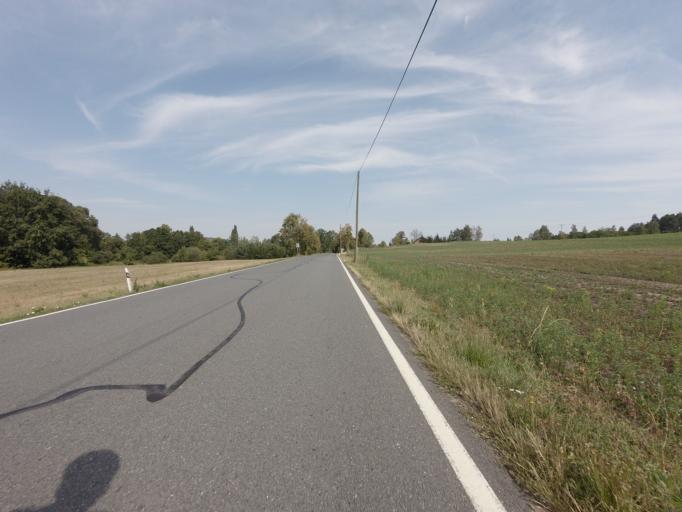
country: CZ
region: Central Bohemia
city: Petrovice
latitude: 49.5478
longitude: 14.3452
